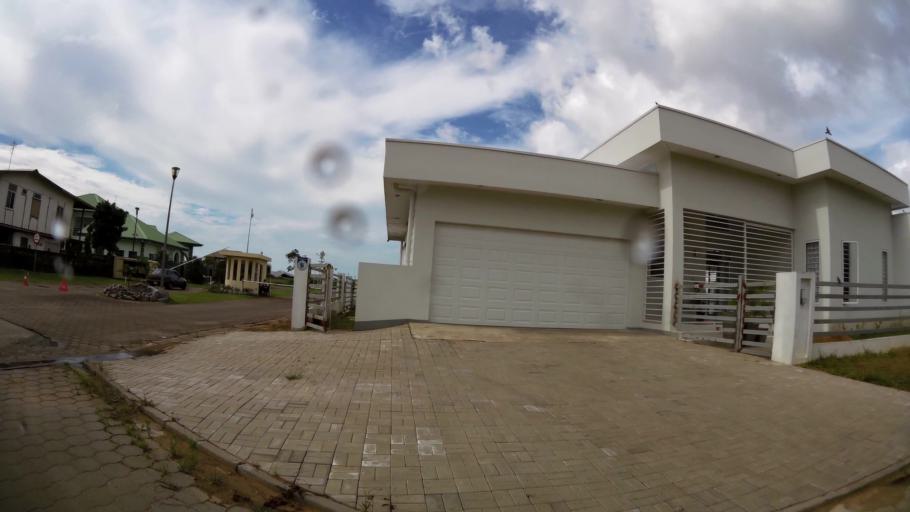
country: SR
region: Paramaribo
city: Paramaribo
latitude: 5.8473
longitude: -55.1927
